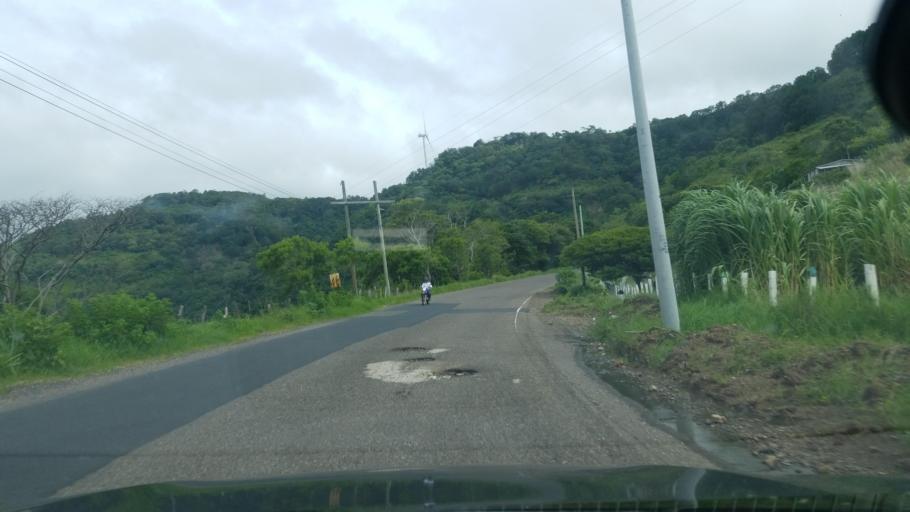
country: HN
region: Choluteca
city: Corpus
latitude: 13.3699
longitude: -86.9400
